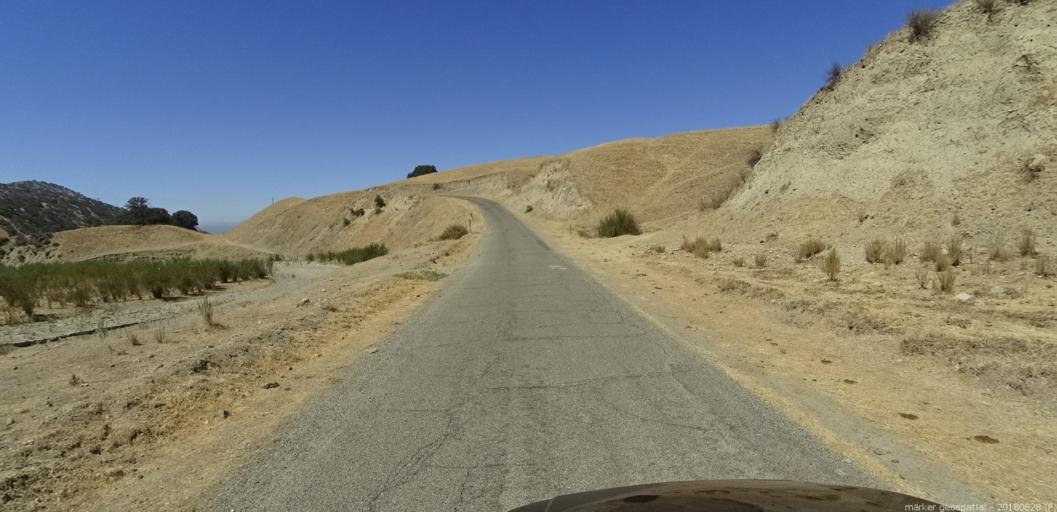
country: US
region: California
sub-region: San Luis Obispo County
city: San Miguel
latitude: 36.0685
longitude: -120.7751
